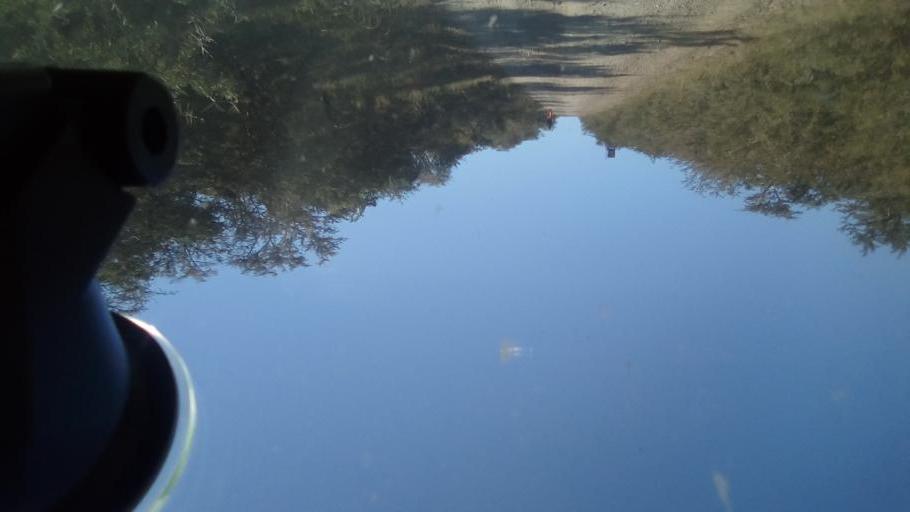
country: ZA
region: Eastern Cape
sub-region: Buffalo City Metropolitan Municipality
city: Bhisho
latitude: -32.7540
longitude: 27.3372
